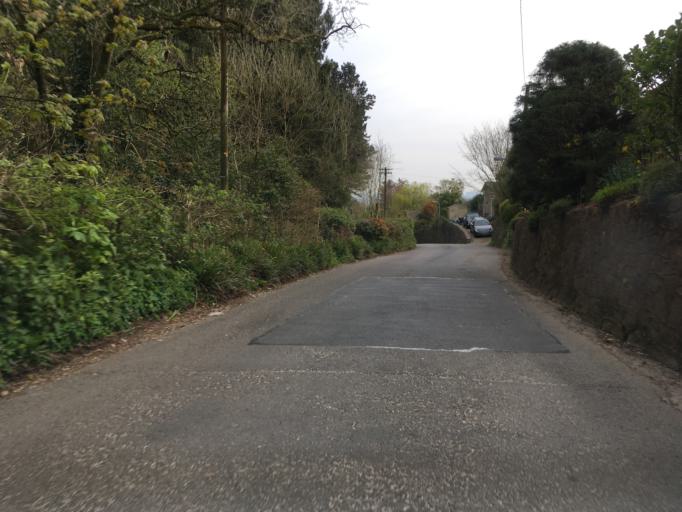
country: GB
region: Wales
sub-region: Cardiff
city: Radyr
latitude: 51.5353
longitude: -3.2300
